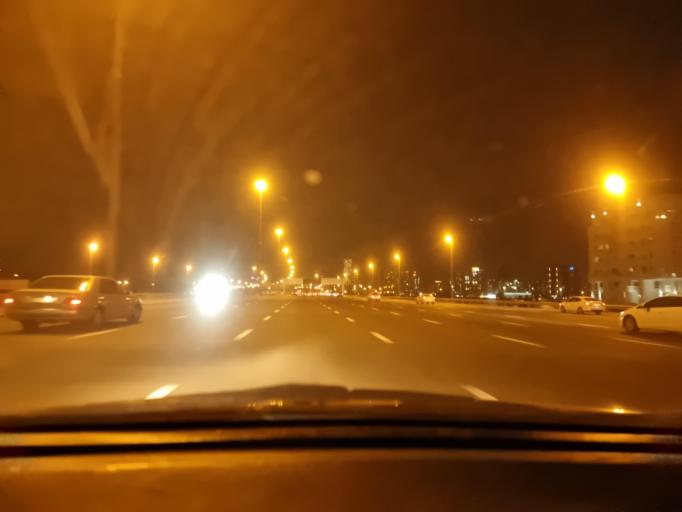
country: AE
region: Dubai
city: Dubai
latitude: 25.0553
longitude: 55.2383
